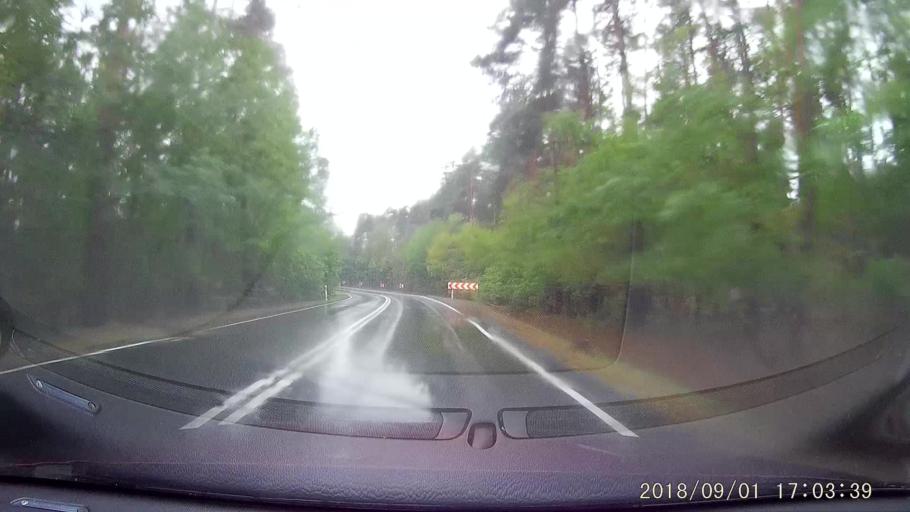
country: PL
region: Lubusz
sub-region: Powiat zielonogorski
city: Swidnica
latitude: 51.8733
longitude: 15.3674
